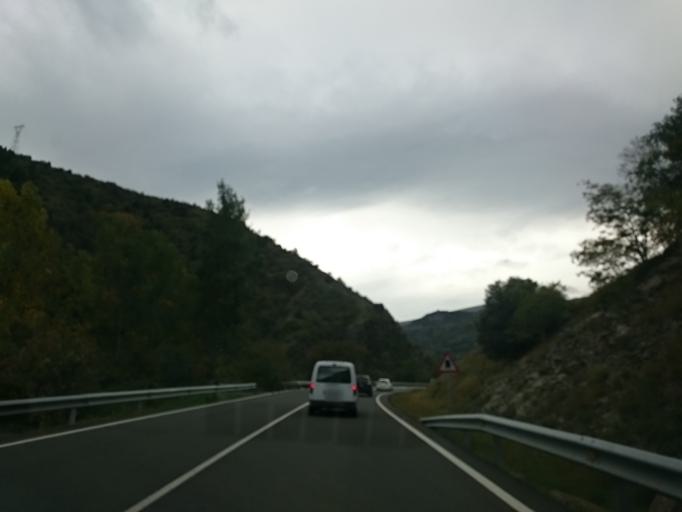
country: ES
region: Catalonia
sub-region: Provincia de Lleida
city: Sort
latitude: 42.4485
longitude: 1.1437
